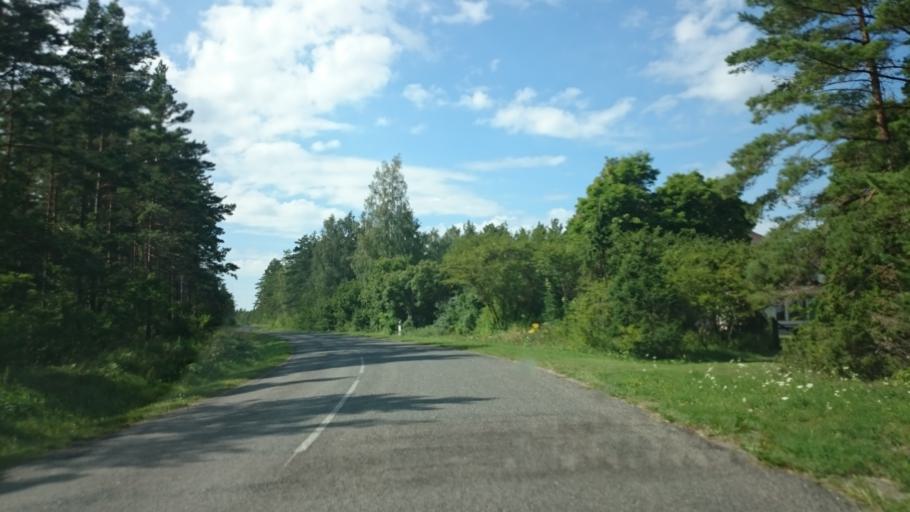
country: EE
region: Saare
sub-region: Orissaare vald
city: Orissaare
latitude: 58.5943
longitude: 23.0033
